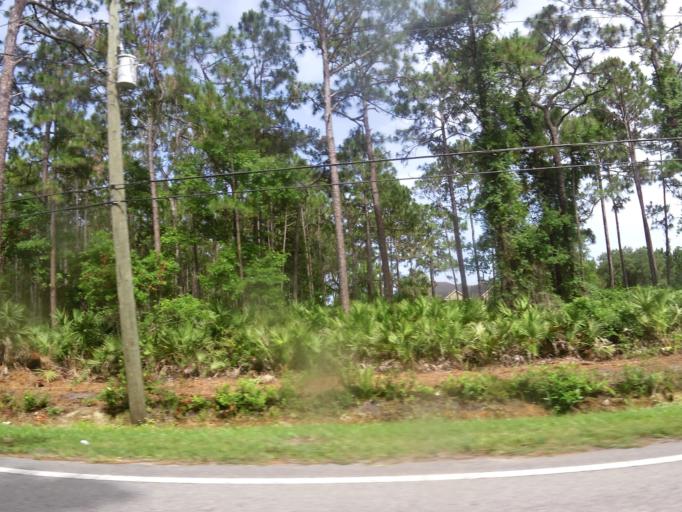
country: US
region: Florida
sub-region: Saint Johns County
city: Saint Augustine
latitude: 29.8771
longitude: -81.3621
